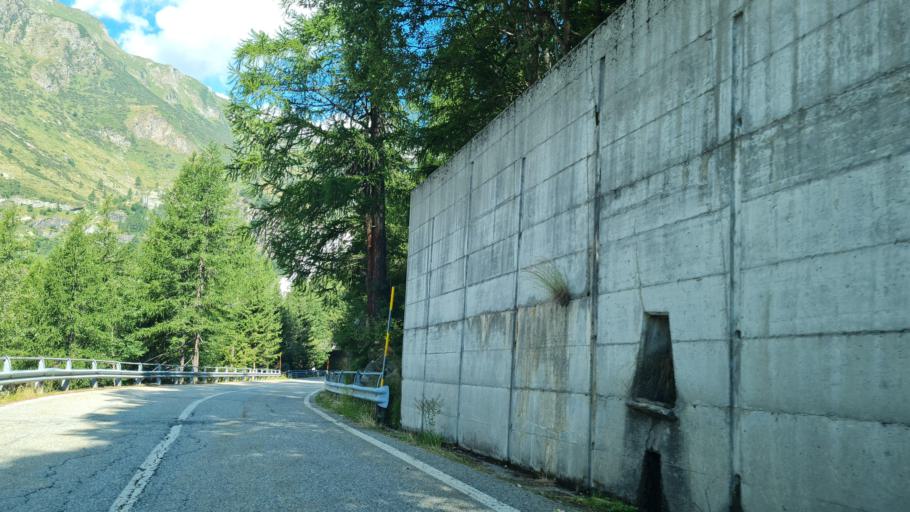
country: IT
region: Piedmont
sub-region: Provincia Verbano-Cusio-Ossola
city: Formazza
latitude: 46.4034
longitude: 8.4207
